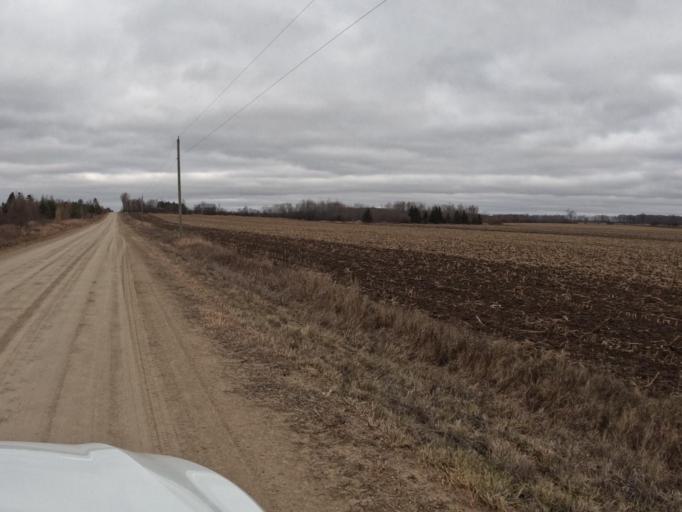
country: CA
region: Ontario
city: Shelburne
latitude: 43.9360
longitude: -80.3934
